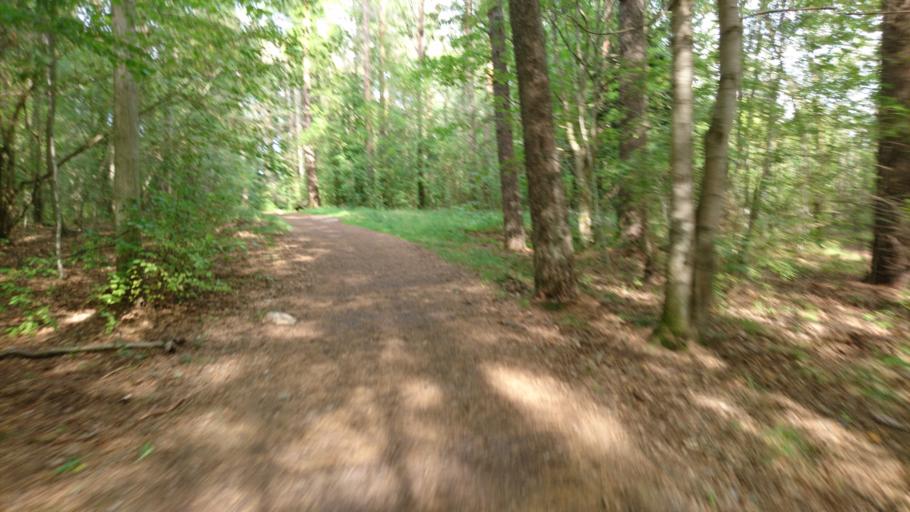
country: SE
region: Uppsala
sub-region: Uppsala Kommun
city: Uppsala
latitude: 59.8449
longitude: 17.6211
